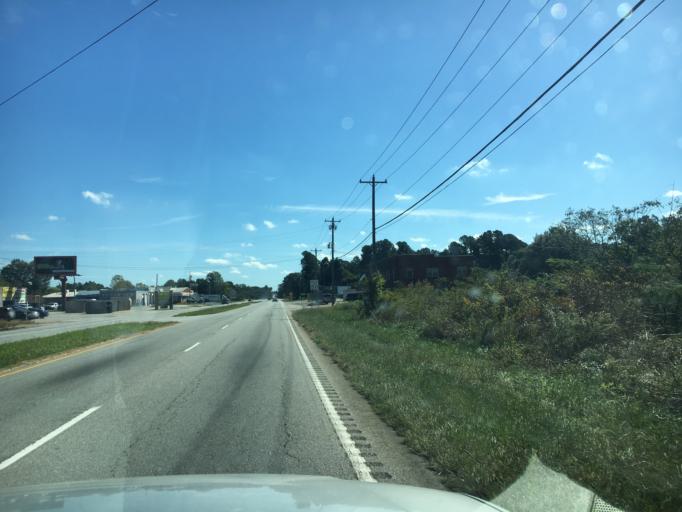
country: US
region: South Carolina
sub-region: Spartanburg County
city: Fairforest
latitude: 34.9384
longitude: -82.0331
